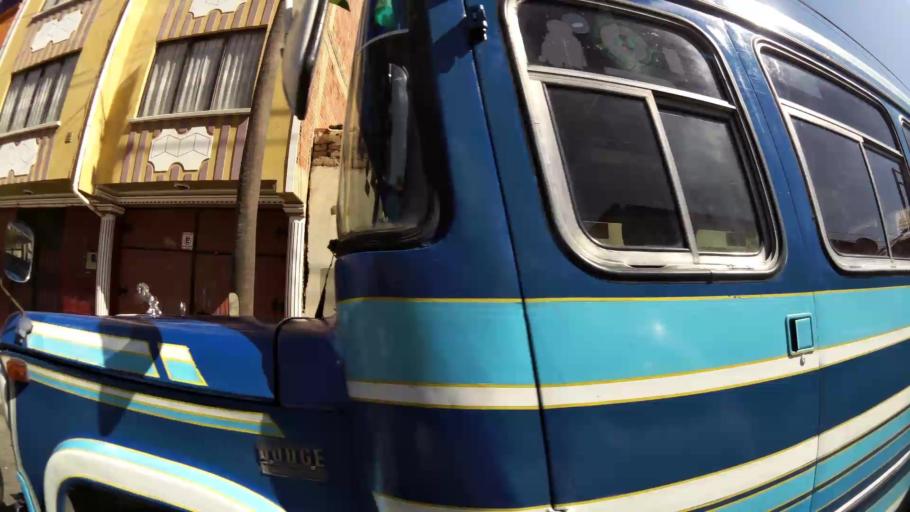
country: BO
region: La Paz
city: La Paz
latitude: -16.5212
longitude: -68.1563
